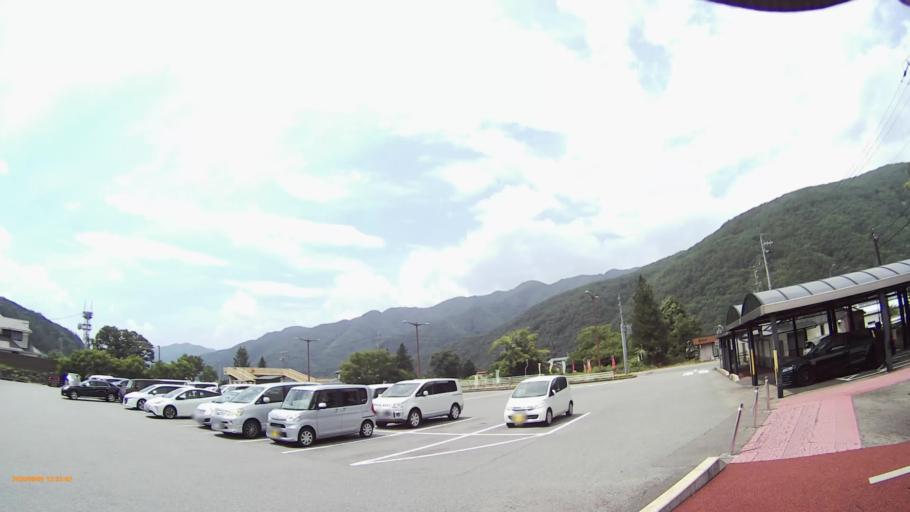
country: JP
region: Nagano
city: Ina
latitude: 35.8667
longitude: 137.7400
